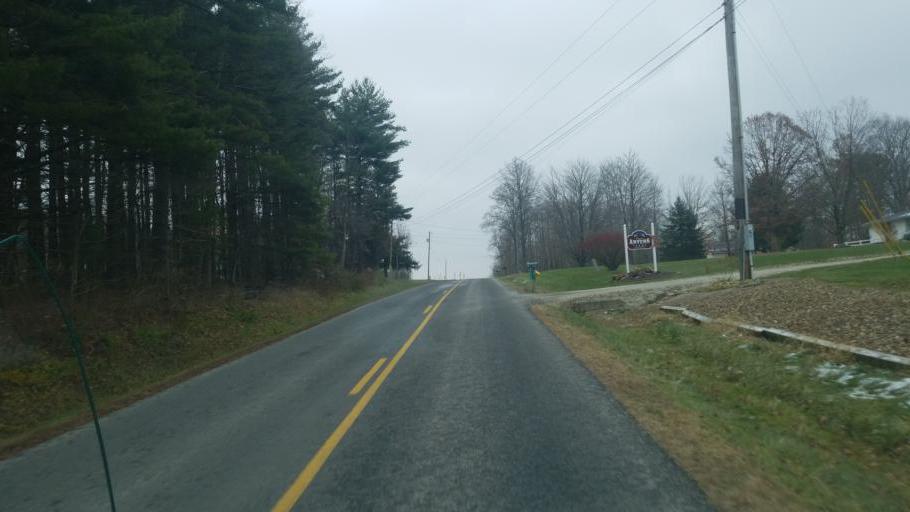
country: US
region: Ohio
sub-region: Medina County
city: Lodi
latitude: 41.1124
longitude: -82.0133
